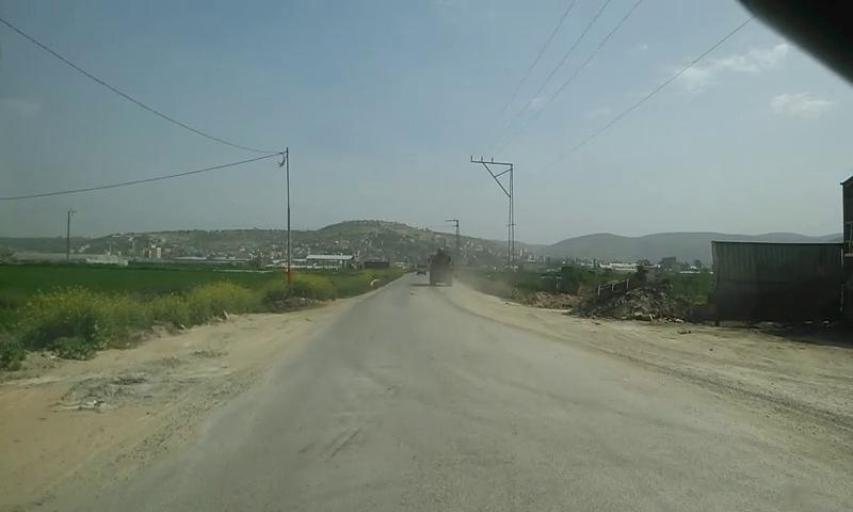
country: PS
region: West Bank
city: Ash Shuhada'
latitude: 32.4370
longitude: 35.2652
